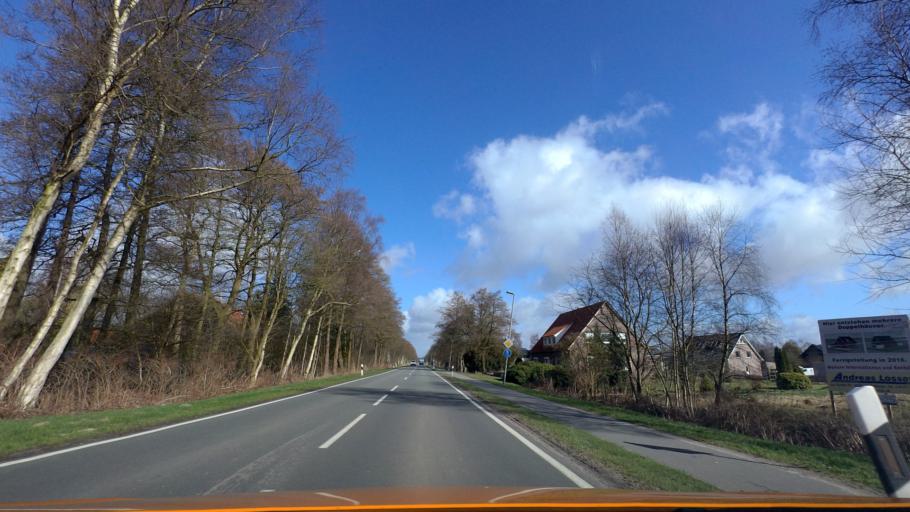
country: DE
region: Lower Saxony
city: Edewecht
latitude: 53.0892
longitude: 7.9412
